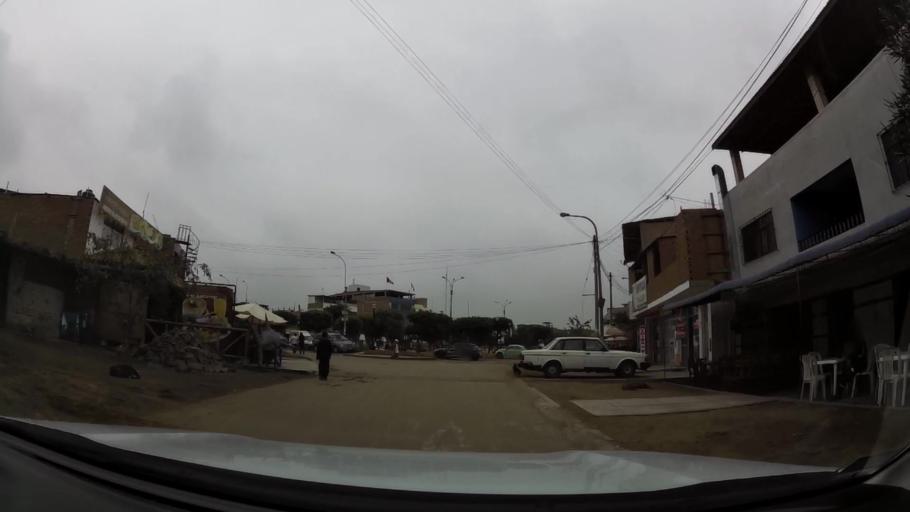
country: PE
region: Lima
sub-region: Lima
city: Punta Hermosa
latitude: -12.2368
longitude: -76.9099
